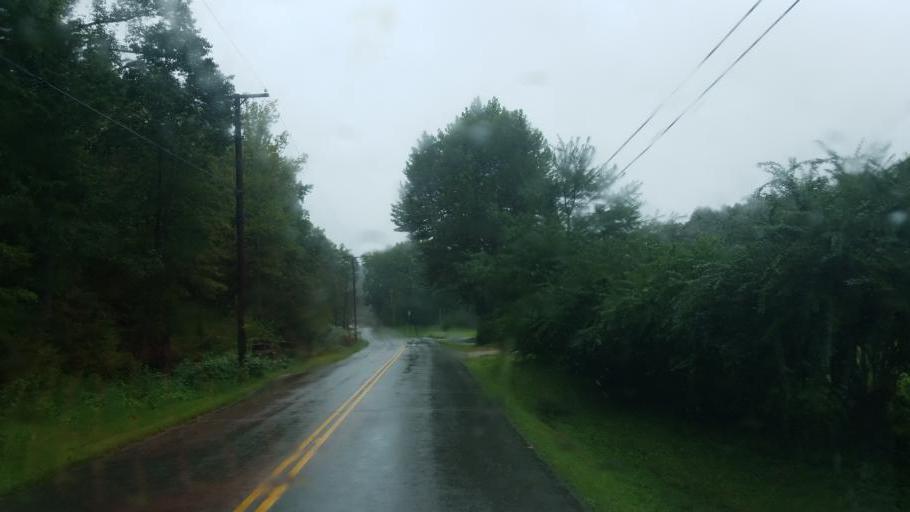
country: US
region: Ohio
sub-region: Scioto County
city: West Portsmouth
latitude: 38.7399
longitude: -83.0726
